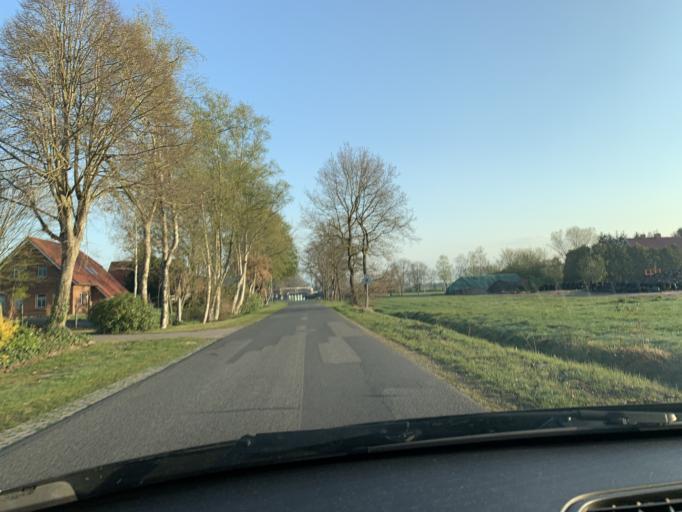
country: DE
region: Lower Saxony
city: Apen
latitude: 53.2888
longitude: 7.8102
